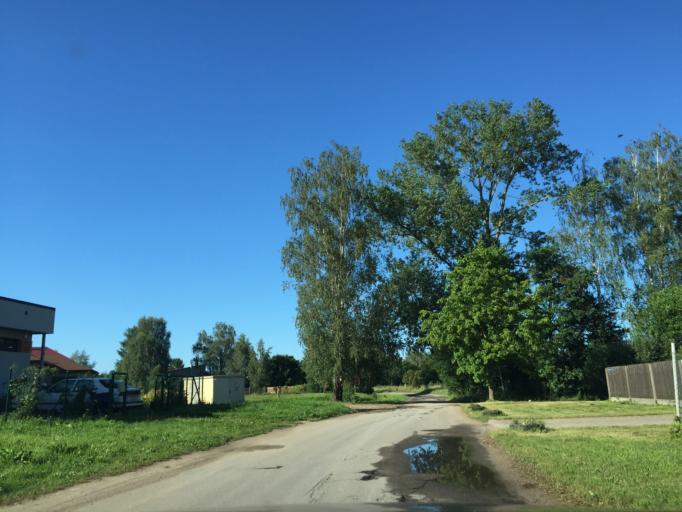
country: LV
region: Riga
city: Jaunciems
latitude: 57.0582
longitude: 24.1386
